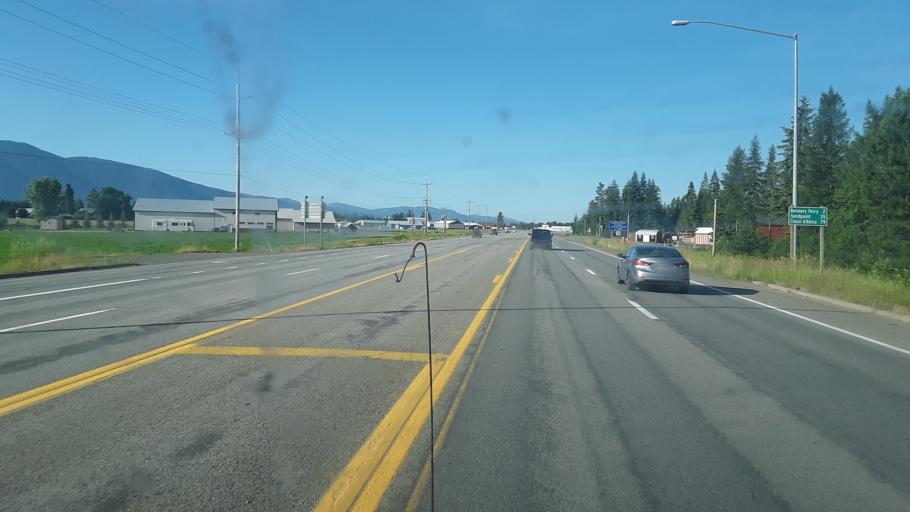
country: US
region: Idaho
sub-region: Boundary County
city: Bonners Ferry
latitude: 48.7299
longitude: -116.3009
